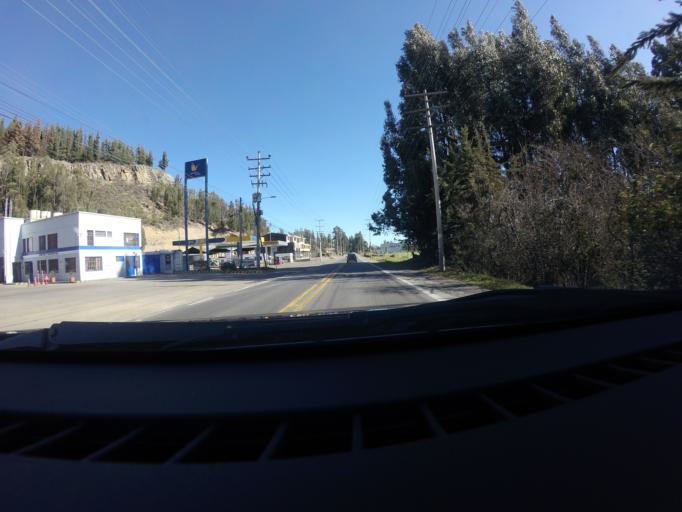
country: CO
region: Cundinamarca
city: Ubate
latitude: 5.2923
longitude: -73.8162
